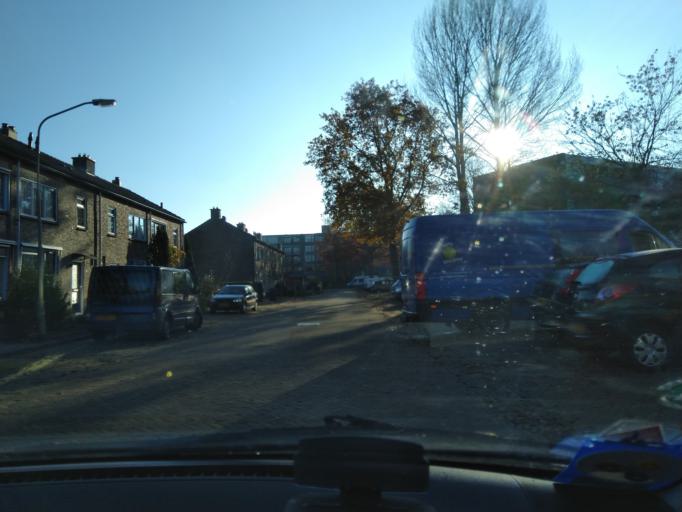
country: NL
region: Drenthe
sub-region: Gemeente Assen
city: Assen
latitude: 53.0055
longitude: 6.5482
